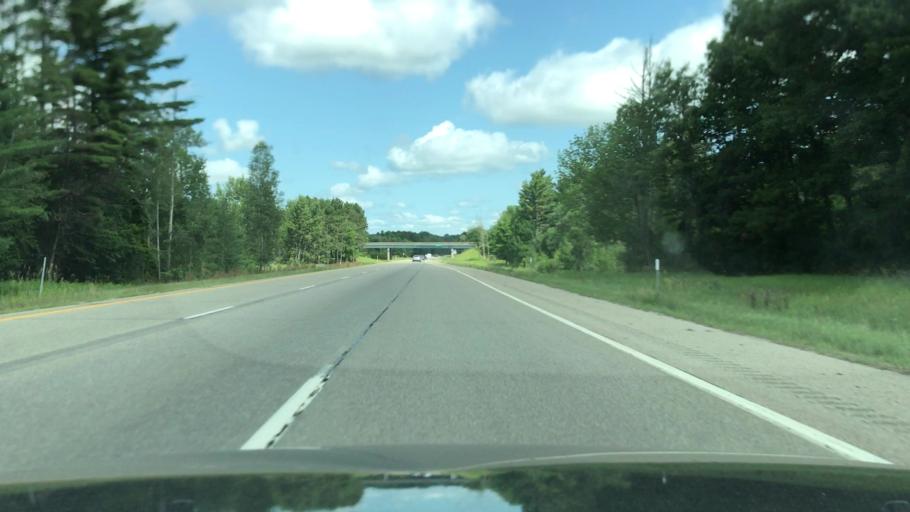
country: US
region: Michigan
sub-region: Mecosta County
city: Big Rapids
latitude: 43.6923
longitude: -85.5231
